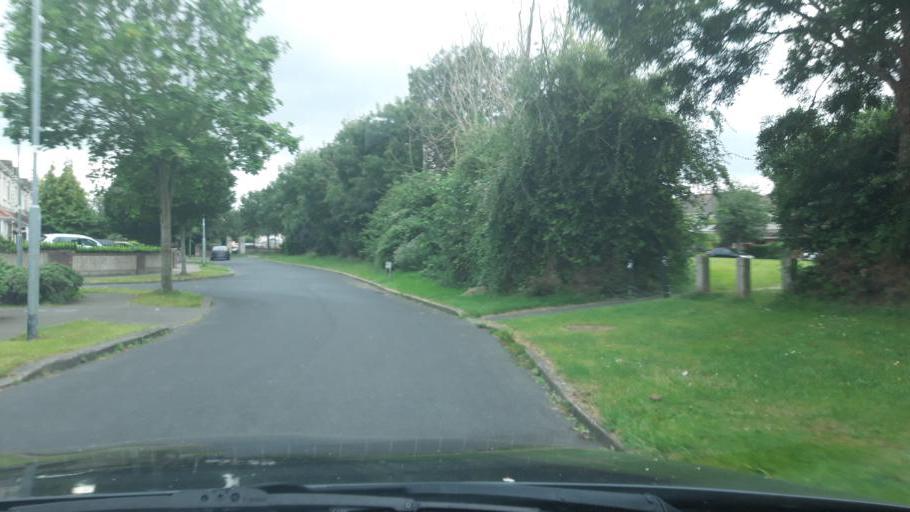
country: IE
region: Leinster
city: Hartstown
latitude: 53.4050
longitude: -6.4119
